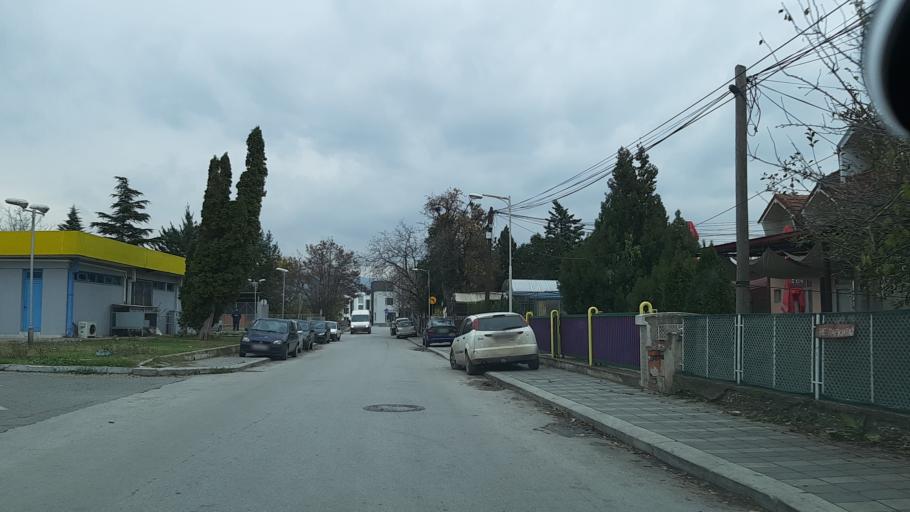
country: MK
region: Kisela Voda
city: Usje
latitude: 41.9780
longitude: 21.4670
